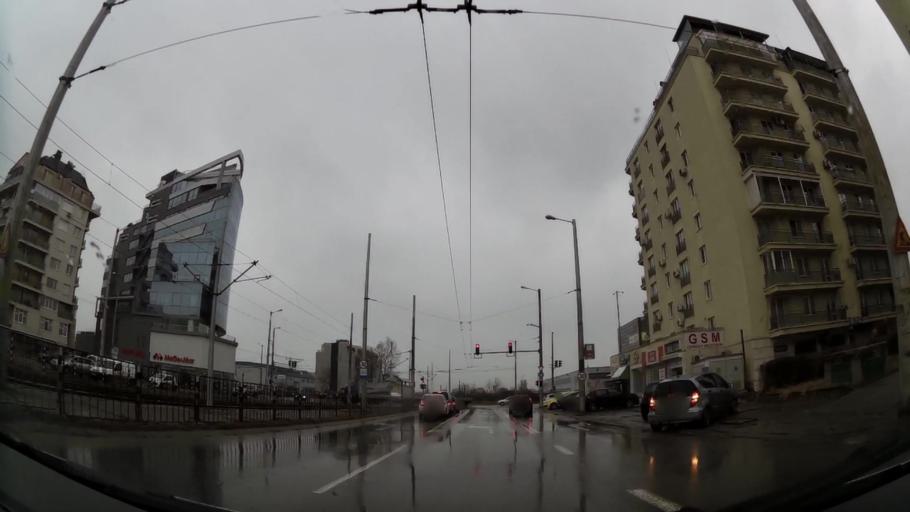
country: BG
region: Sofia-Capital
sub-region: Stolichna Obshtina
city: Sofia
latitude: 42.6507
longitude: 23.4055
